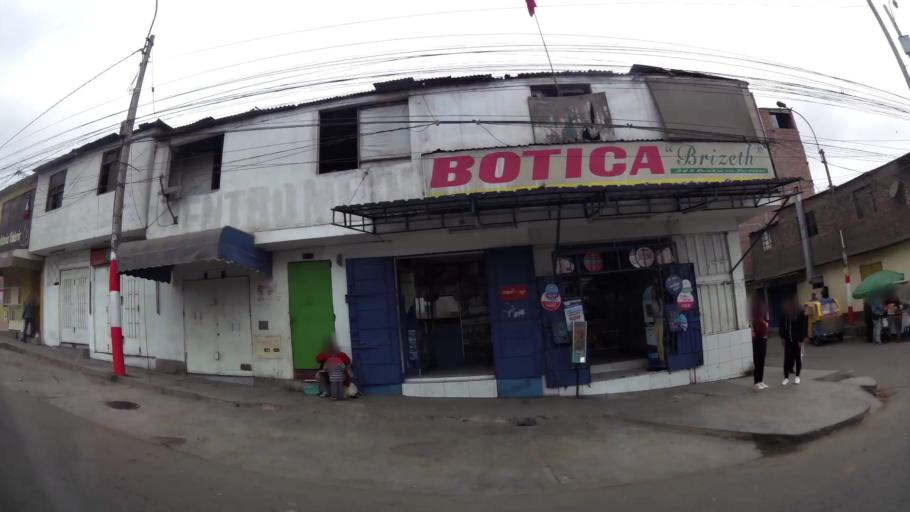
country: PE
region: Lima
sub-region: Lima
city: Surco
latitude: -12.1365
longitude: -76.9597
